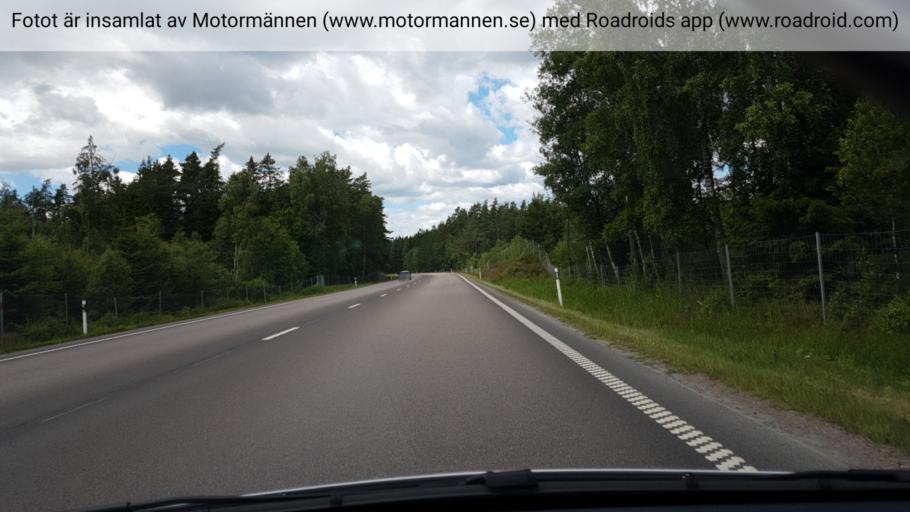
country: SE
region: Vaestra Goetaland
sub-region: Skara Kommun
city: Skara
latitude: 58.4159
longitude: 13.3659
